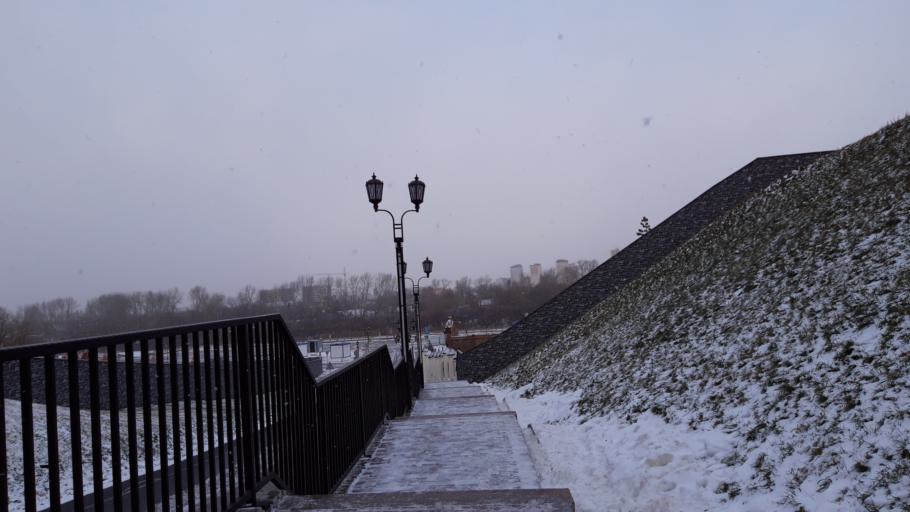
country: RU
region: Tjumen
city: Tyumen
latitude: 57.1608
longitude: 65.5507
